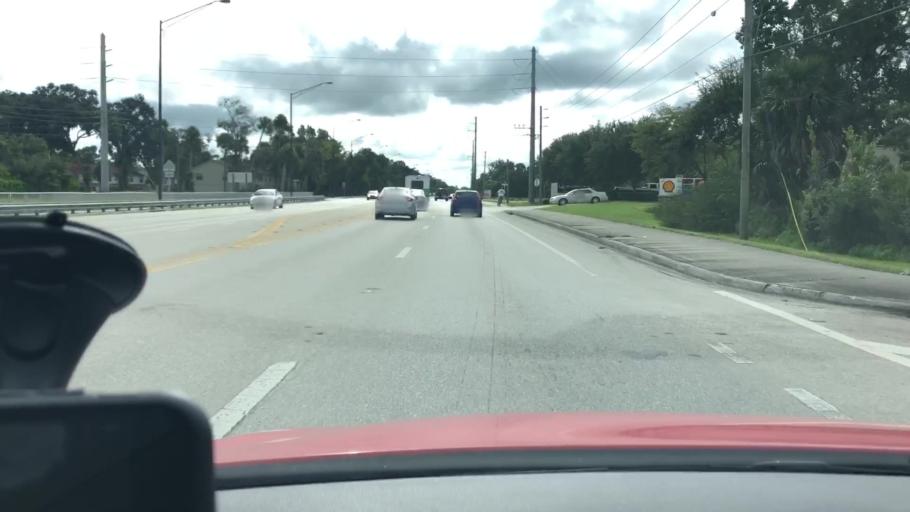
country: US
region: Florida
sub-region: Volusia County
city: Port Orange
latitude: 29.1372
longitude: -81.0107
